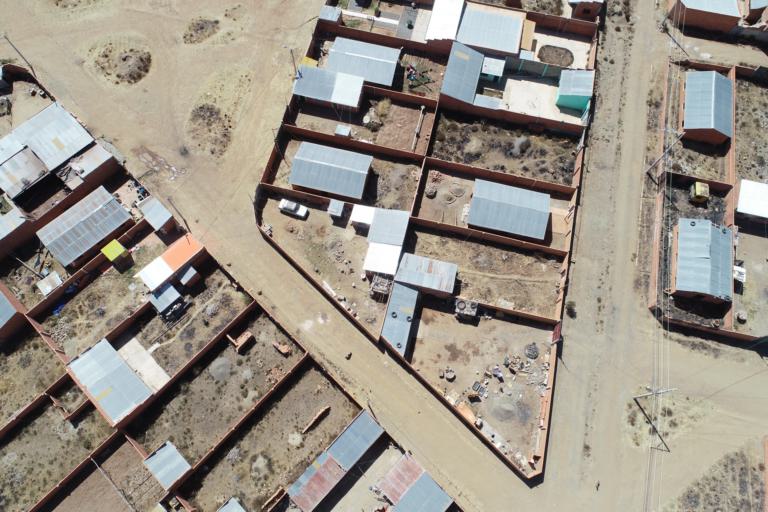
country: BO
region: La Paz
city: La Paz
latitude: -16.5927
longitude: -68.2123
